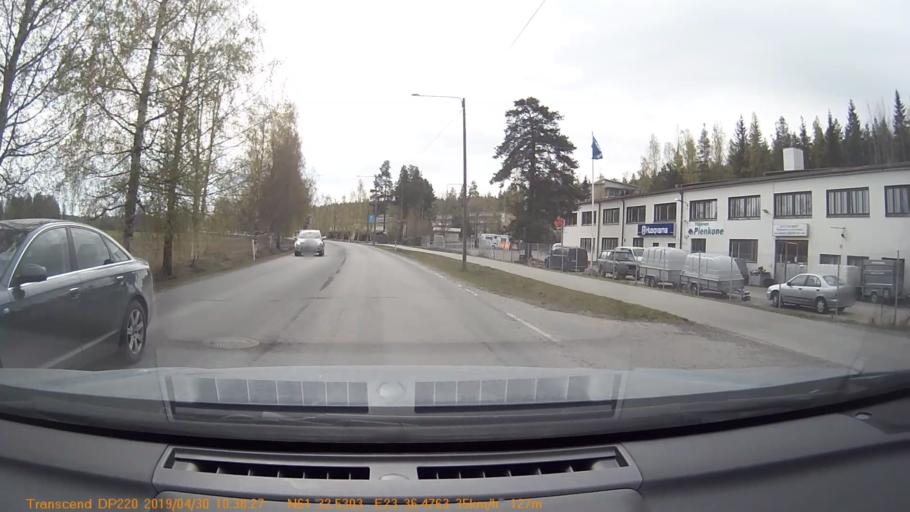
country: FI
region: Pirkanmaa
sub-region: Tampere
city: Yloejaervi
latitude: 61.5423
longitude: 23.6081
